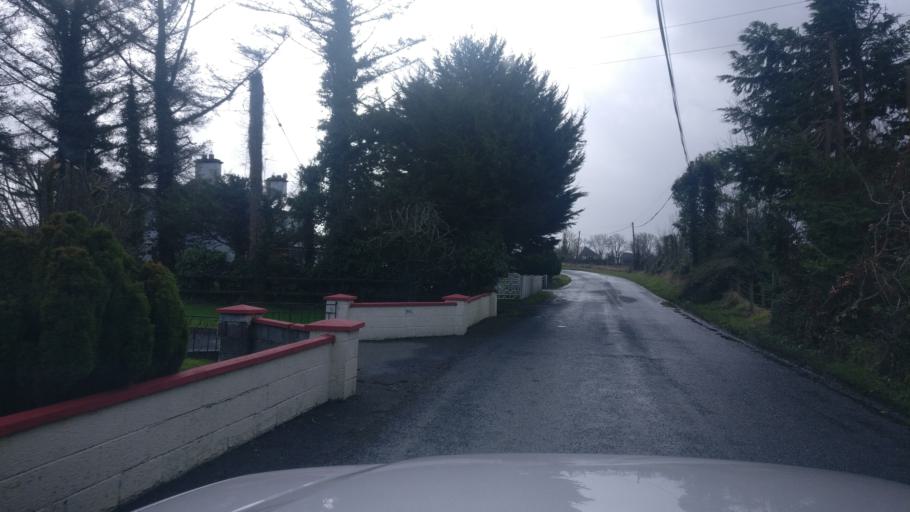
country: IE
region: Connaught
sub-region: County Galway
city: Loughrea
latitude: 53.2977
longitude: -8.4816
